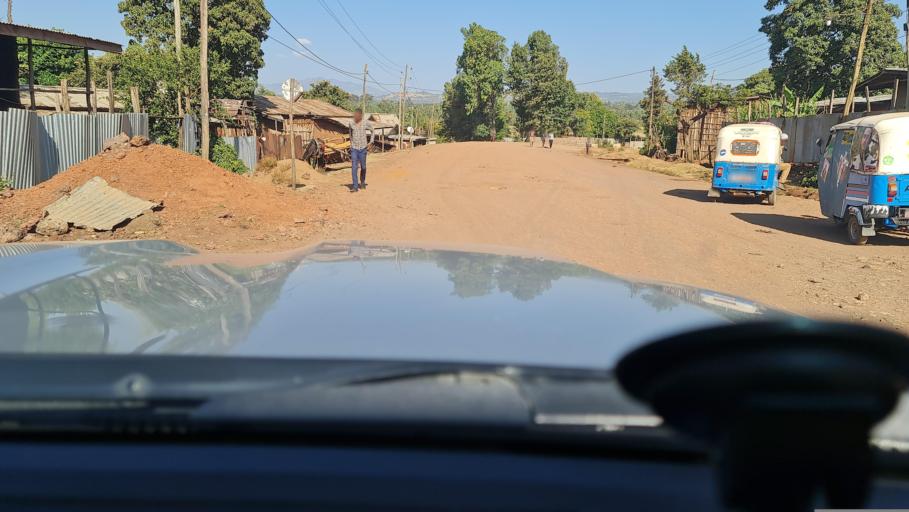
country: ET
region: Oromiya
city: Waliso
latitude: 8.6087
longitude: 37.9230
